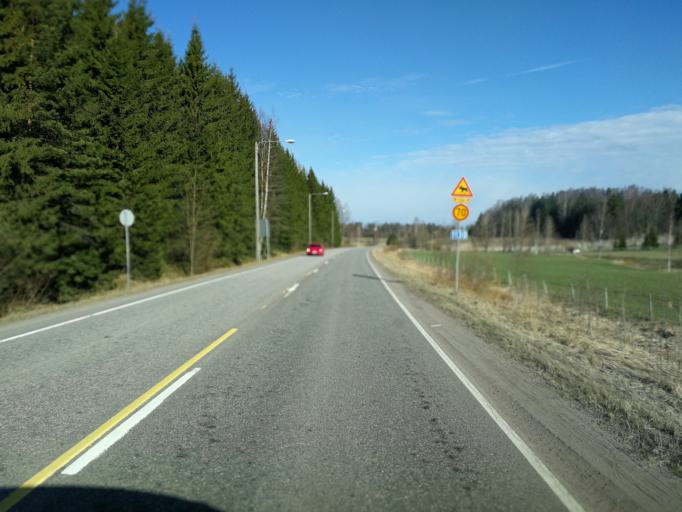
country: FI
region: Uusimaa
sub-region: Helsinki
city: Espoo
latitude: 60.1919
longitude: 24.5689
